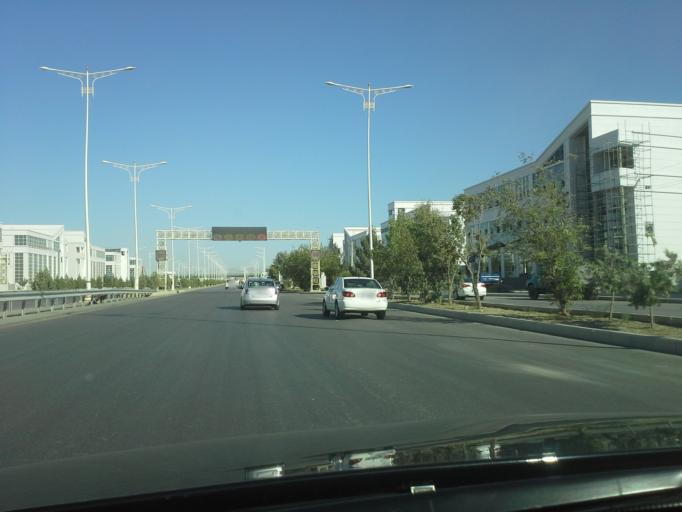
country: TM
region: Ahal
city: Ashgabat
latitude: 37.9647
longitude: 58.4122
